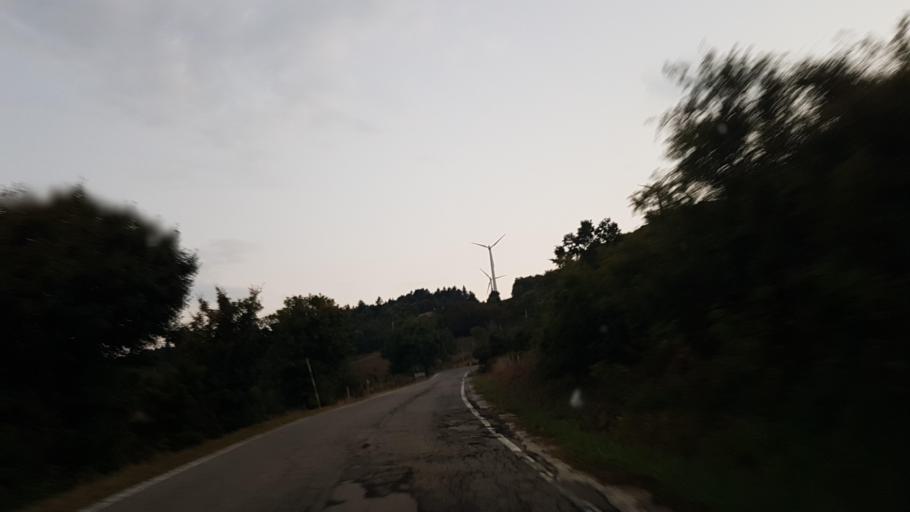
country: IT
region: Emilia-Romagna
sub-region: Provincia di Parma
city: Tornolo
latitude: 44.4305
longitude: 9.6237
